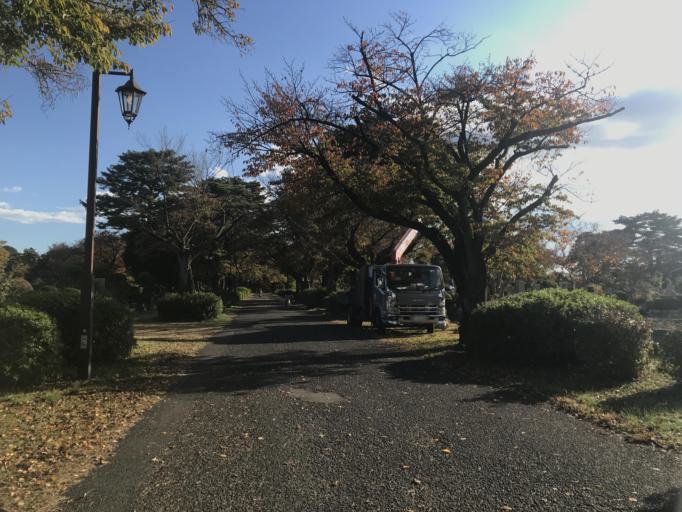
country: JP
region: Tokyo
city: Higashimurayama-shi
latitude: 35.7437
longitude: 139.4879
